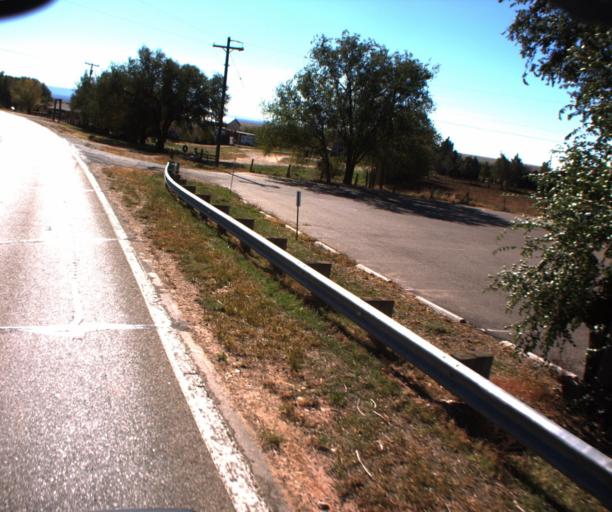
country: US
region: Arizona
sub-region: Coconino County
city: Fredonia
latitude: 36.9419
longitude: -112.5252
